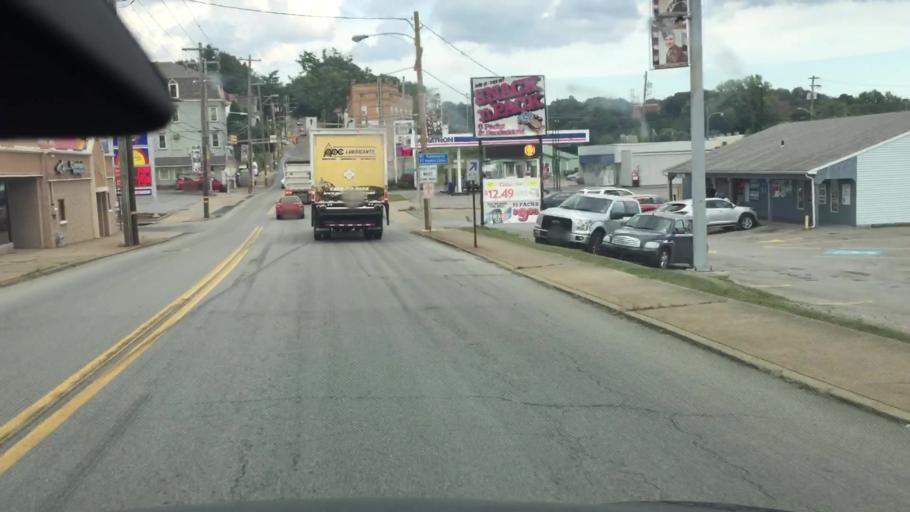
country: US
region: Pennsylvania
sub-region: Butler County
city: Butler
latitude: 40.8610
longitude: -79.8928
